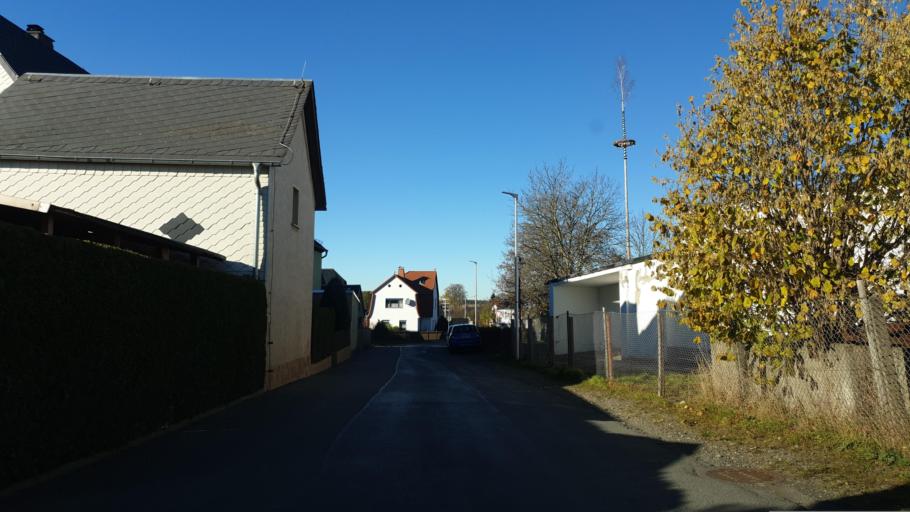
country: DE
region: Saxony
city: Elsterberg
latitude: 50.6384
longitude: 12.1534
